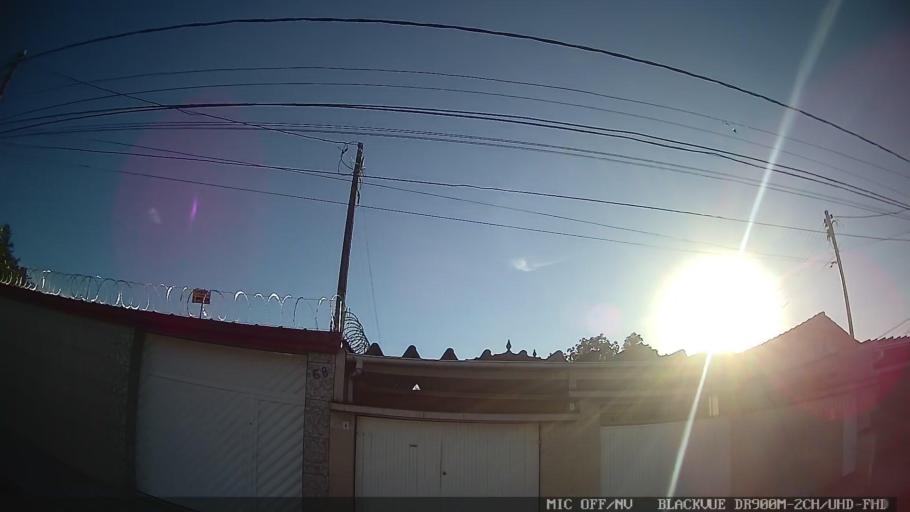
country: BR
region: Sao Paulo
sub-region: Santos
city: Santos
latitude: -23.9391
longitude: -46.2931
